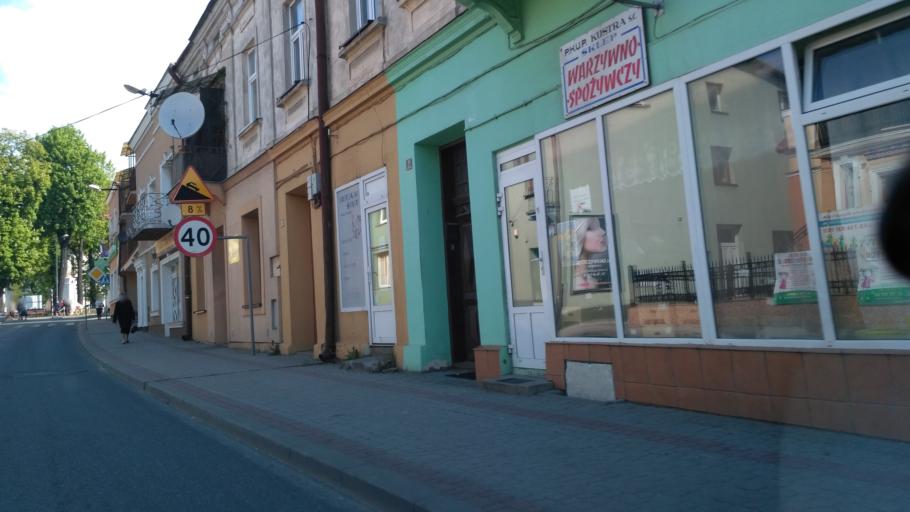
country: PL
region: Subcarpathian Voivodeship
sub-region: Powiat rzeszowski
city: Dynow
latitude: 49.8140
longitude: 22.2321
